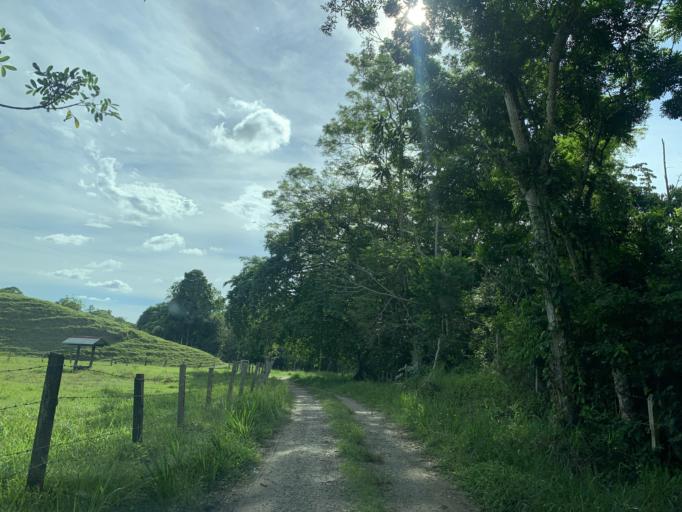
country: CO
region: Boyaca
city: Puerto Boyaca
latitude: 6.0114
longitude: -74.3924
